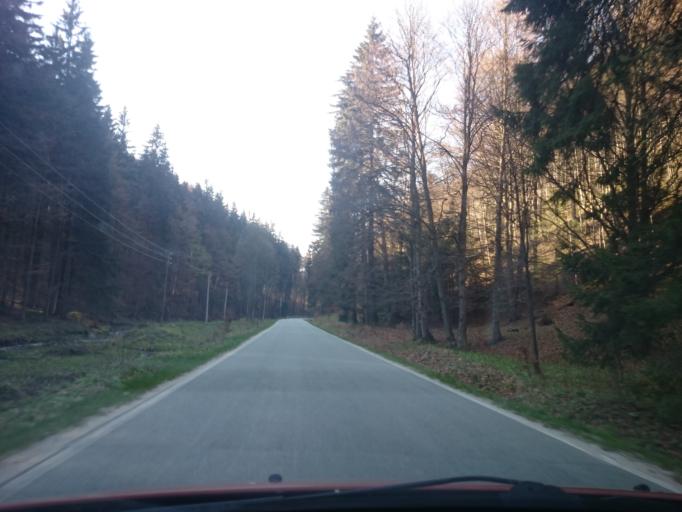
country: PL
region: Lower Silesian Voivodeship
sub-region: Powiat klodzki
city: Duszniki-Zdroj
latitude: 50.3515
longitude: 16.3975
